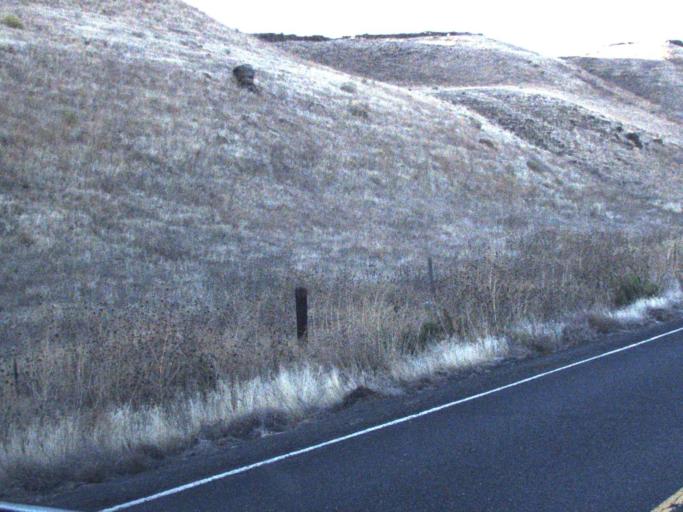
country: US
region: Washington
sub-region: Walla Walla County
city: Waitsburg
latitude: 46.6180
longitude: -118.2313
